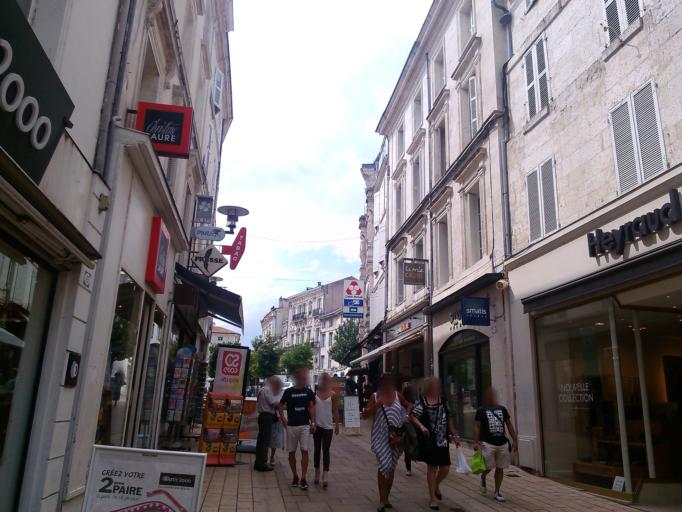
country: FR
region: Poitou-Charentes
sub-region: Departement de la Charente
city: Angouleme
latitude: 45.6488
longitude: 0.1573
